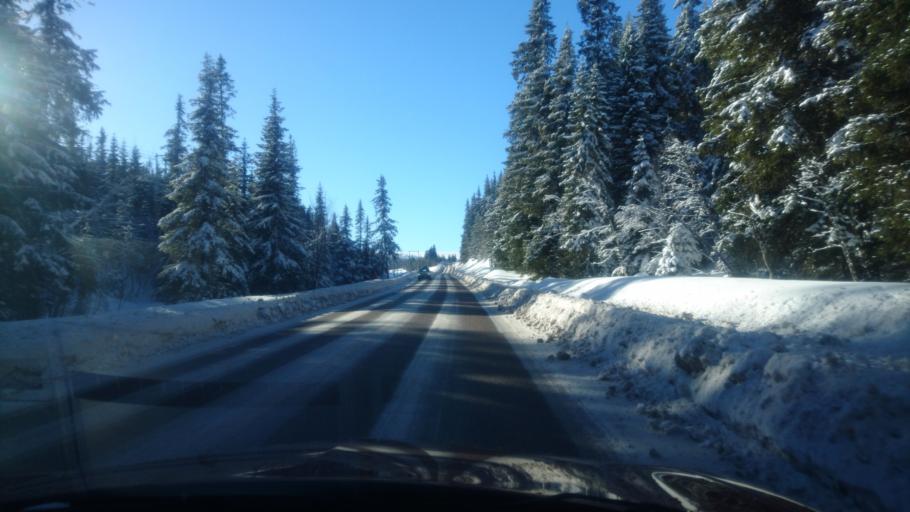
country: SE
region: Dalarna
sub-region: Malung-Saelens kommun
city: Malung
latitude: 61.1658
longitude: 13.1485
